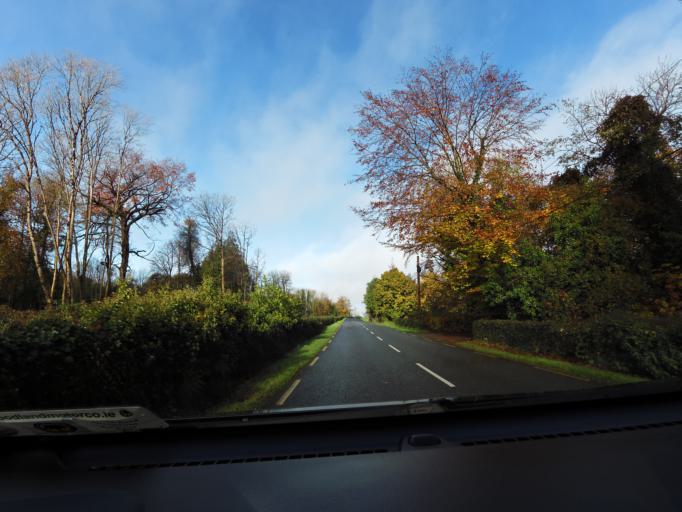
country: IE
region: Leinster
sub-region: An Iarmhi
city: Moate
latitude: 53.3797
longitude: -7.8006
